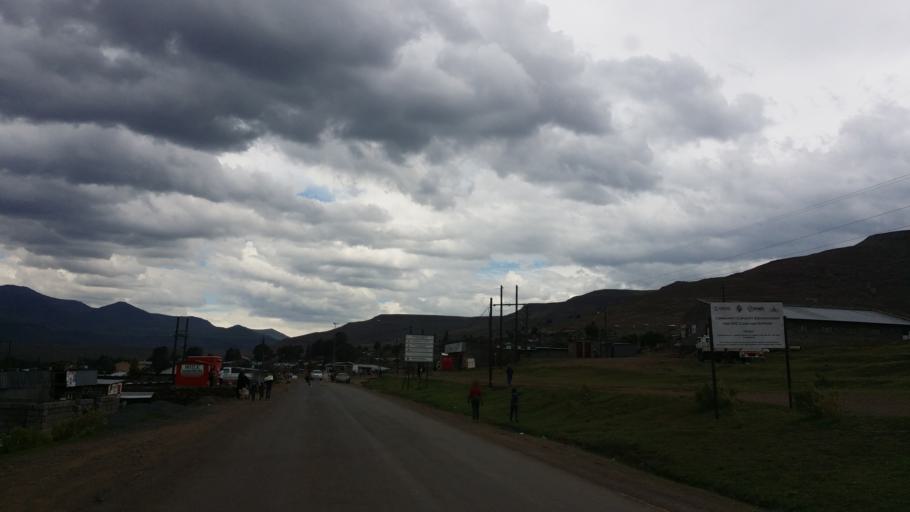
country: LS
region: Mokhotlong
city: Mokhotlong
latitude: -29.2886
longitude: 29.0561
